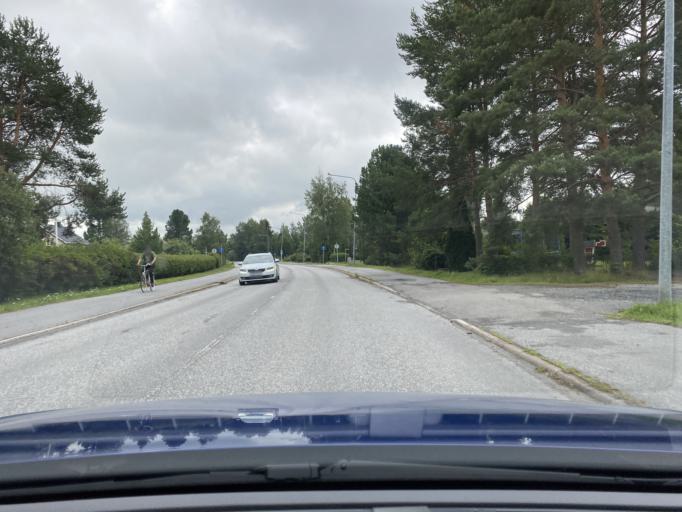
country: FI
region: Ostrobothnia
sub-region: Kyroenmaa
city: Laihia
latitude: 62.9723
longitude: 22.0221
